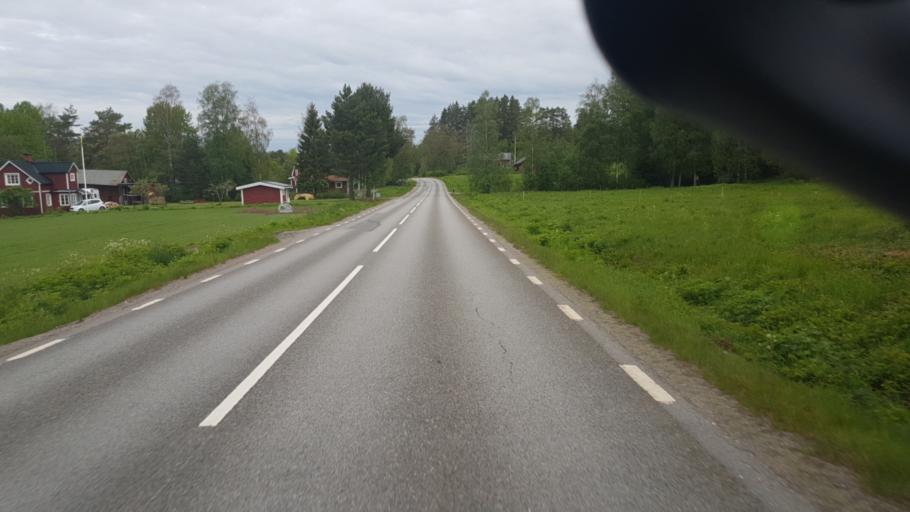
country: SE
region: Vaermland
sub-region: Arvika Kommun
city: Arvika
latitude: 59.7347
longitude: 12.5611
